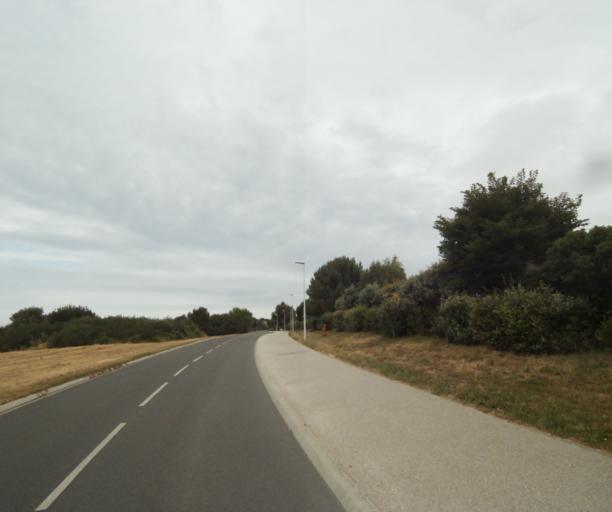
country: FR
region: Pays de la Loire
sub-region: Departement de la Vendee
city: Chateau-d'Olonne
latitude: 46.4796
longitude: -1.7318
